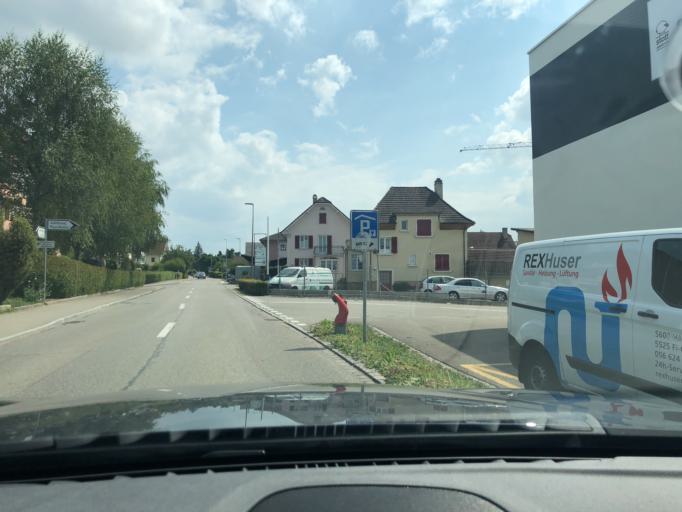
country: CH
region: Aargau
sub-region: Bezirk Bremgarten
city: Bremgarten
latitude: 47.3515
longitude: 8.3504
